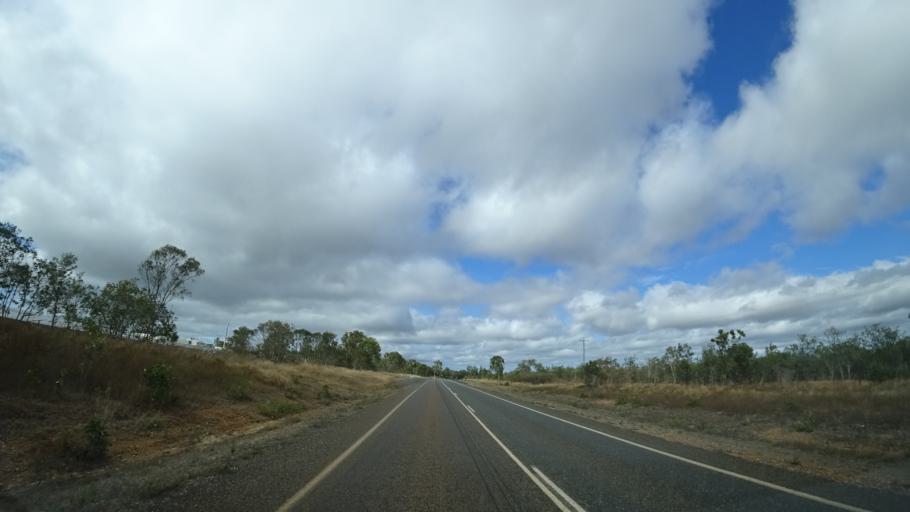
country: AU
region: Queensland
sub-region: Cook
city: Cooktown
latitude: -15.8700
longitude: 144.8600
